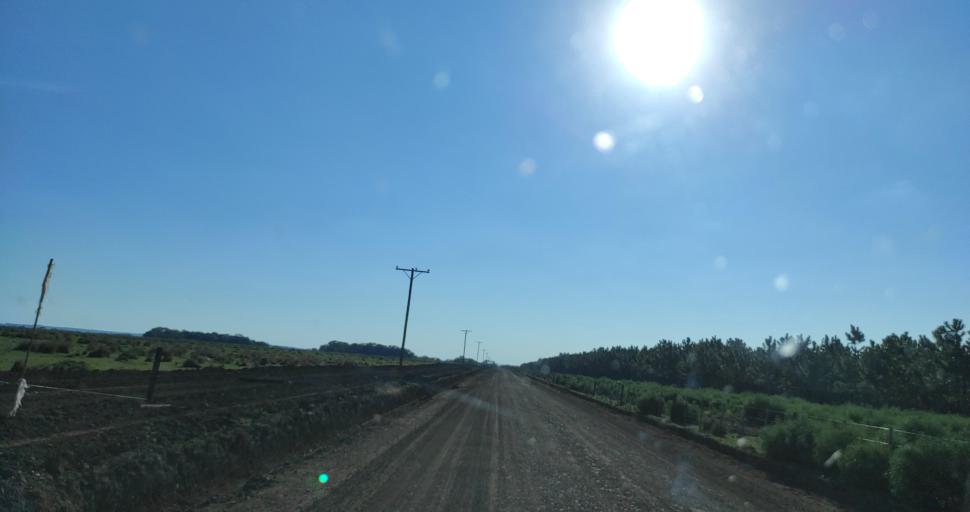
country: PY
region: Itapua
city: San Juan del Parana
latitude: -27.4240
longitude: -56.1109
